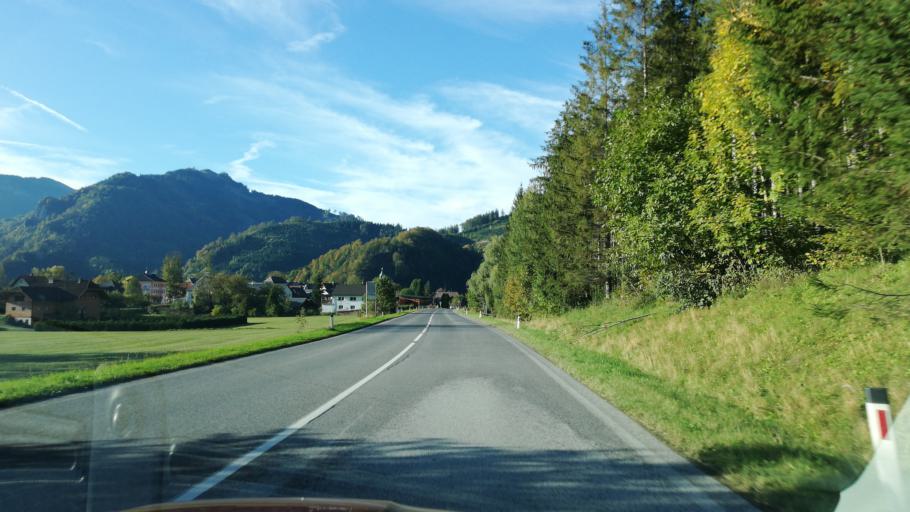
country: AT
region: Styria
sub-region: Politischer Bezirk Liezen
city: Altenmarkt bei Sankt Gallen
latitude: 47.7206
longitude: 14.6536
